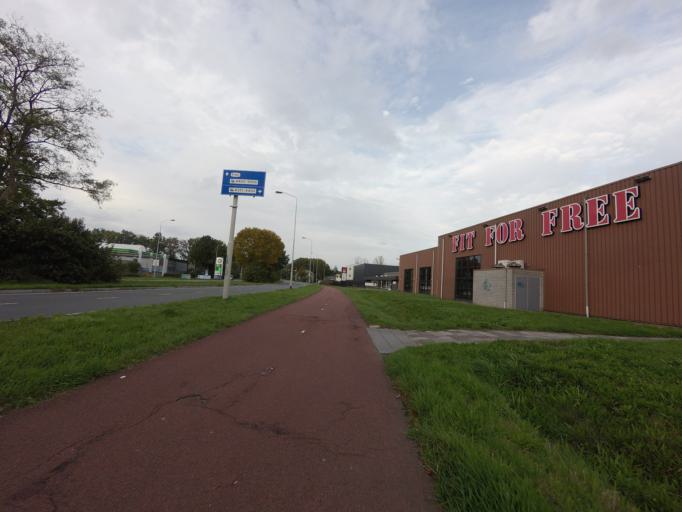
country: NL
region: North Brabant
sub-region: Gemeente Breda
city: Breda
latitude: 51.6103
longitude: 4.7540
